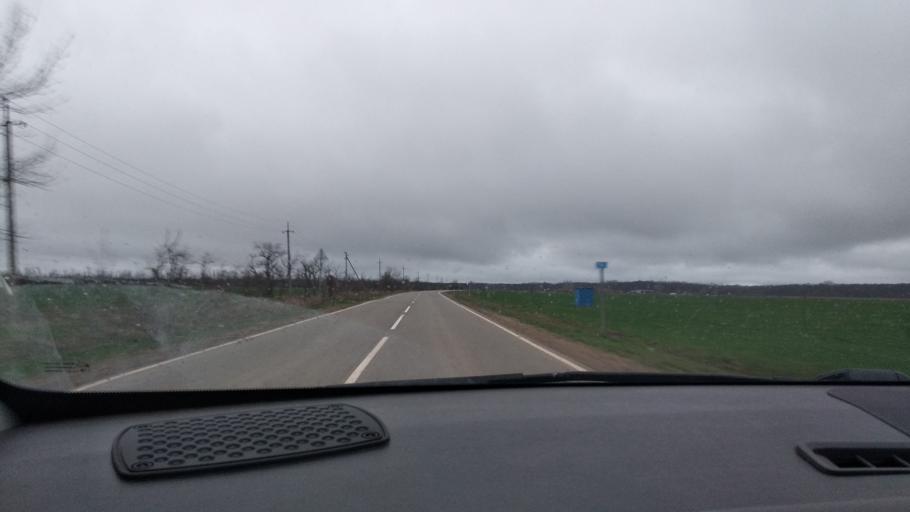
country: RU
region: Krasnodarskiy
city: Afipskiy
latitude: 44.8994
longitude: 38.7853
